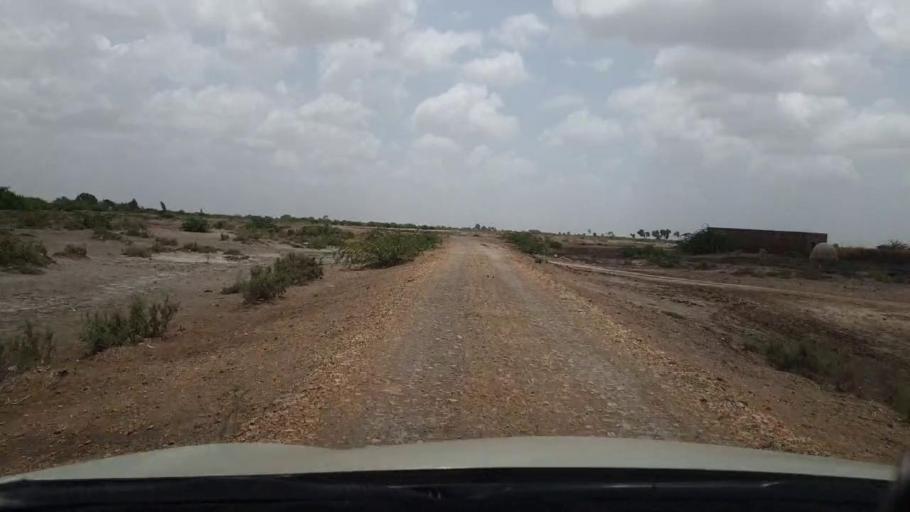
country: PK
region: Sindh
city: Kadhan
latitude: 24.3959
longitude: 68.9360
